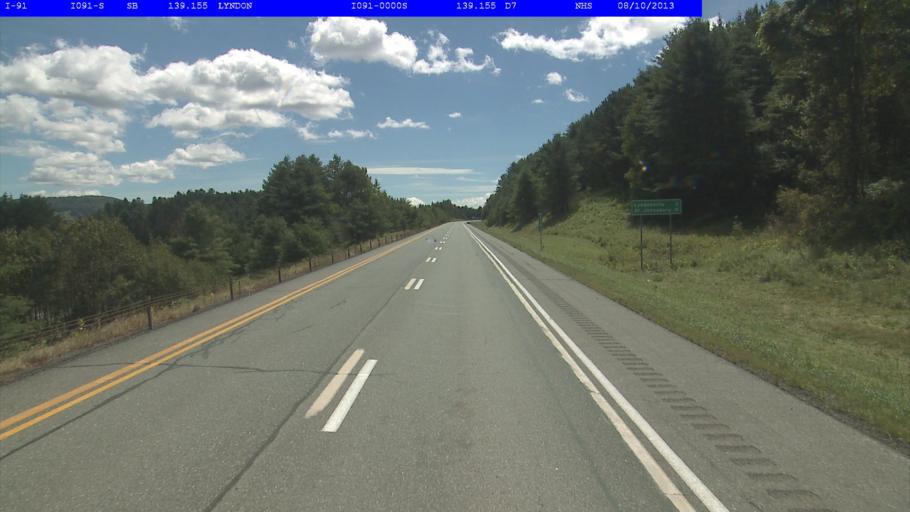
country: US
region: Vermont
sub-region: Caledonia County
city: Lyndonville
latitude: 44.5436
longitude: -72.0240
